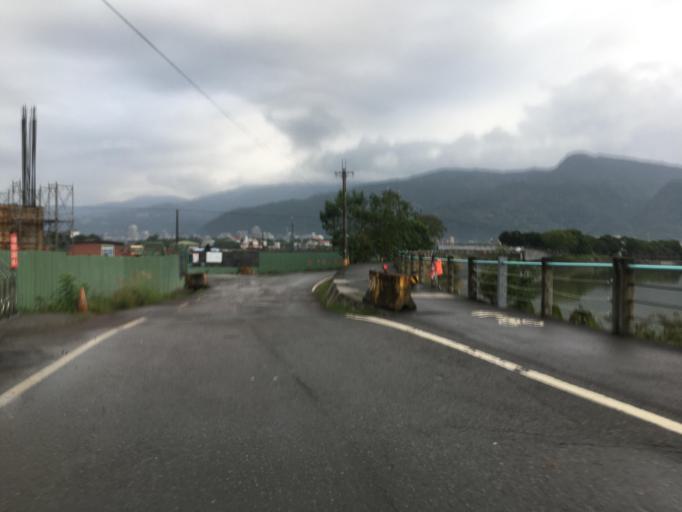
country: TW
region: Taiwan
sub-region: Yilan
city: Yilan
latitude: 24.8292
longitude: 121.8015
